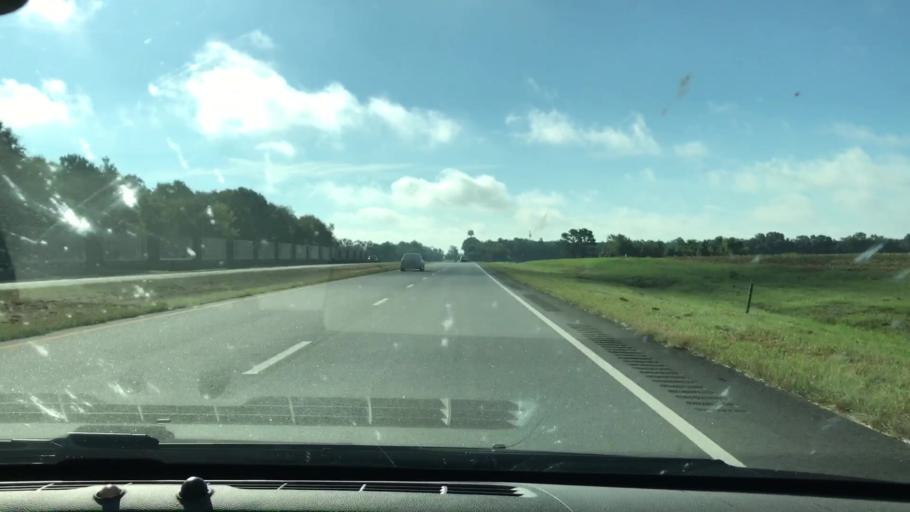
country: US
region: Georgia
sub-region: Terrell County
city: Dawson
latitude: 31.7274
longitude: -84.3602
